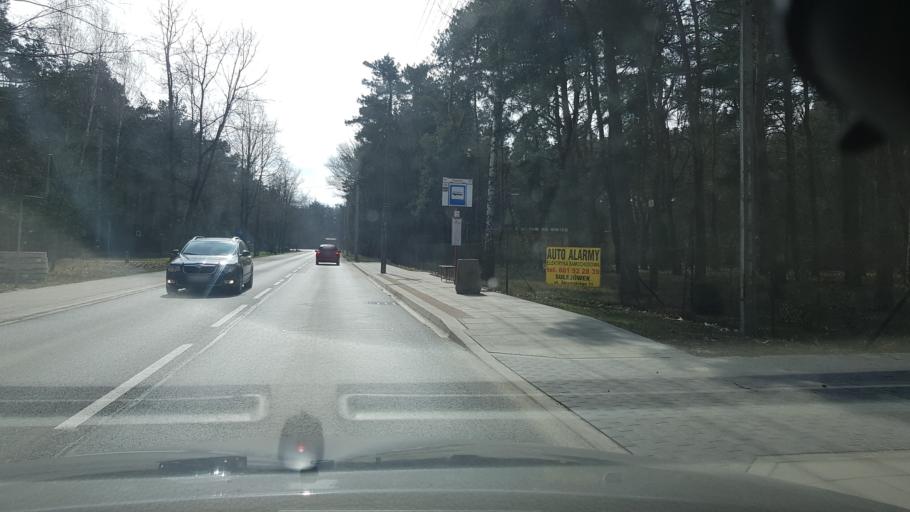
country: PL
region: Masovian Voivodeship
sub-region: Warszawa
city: Wesola
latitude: 52.2391
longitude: 21.2223
